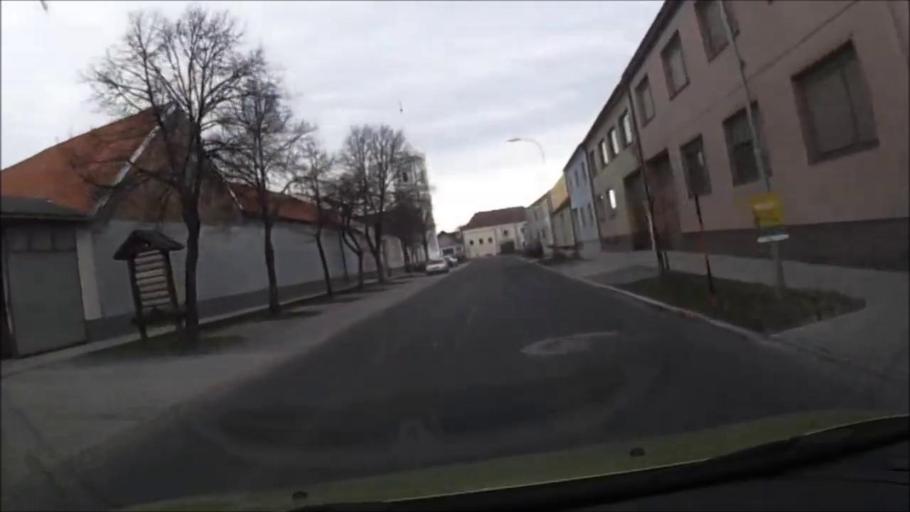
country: AT
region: Burgenland
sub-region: Eisenstadt-Umgebung
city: Leithaprodersdorf
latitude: 47.9376
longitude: 16.4771
